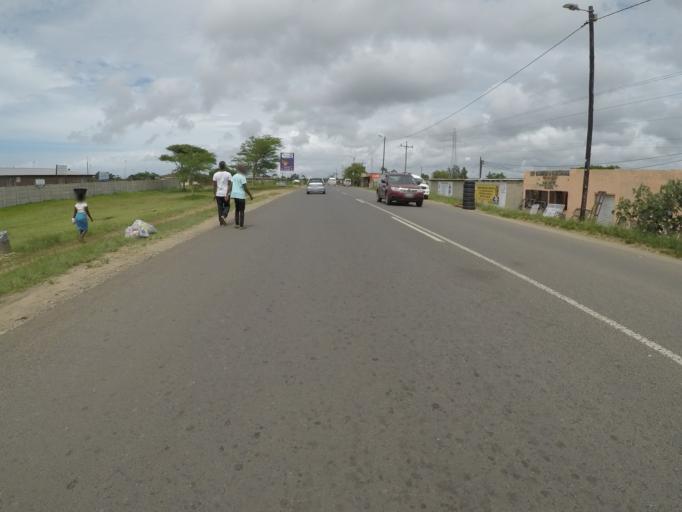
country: ZA
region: KwaZulu-Natal
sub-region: uThungulu District Municipality
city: eSikhawini
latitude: -28.8657
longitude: 31.9087
